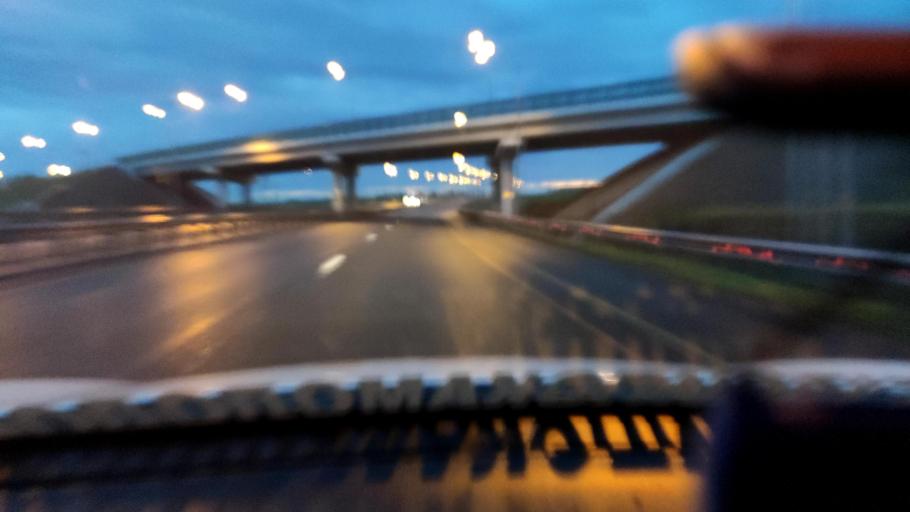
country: RU
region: Rostov
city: Tarasovskiy
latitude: 48.6586
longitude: 40.3593
